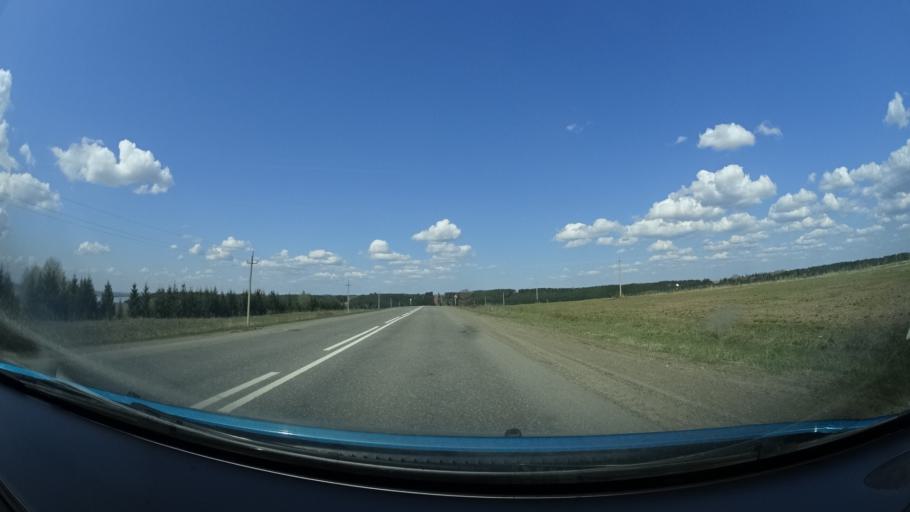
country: RU
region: Perm
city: Osa
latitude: 57.2459
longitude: 55.5917
